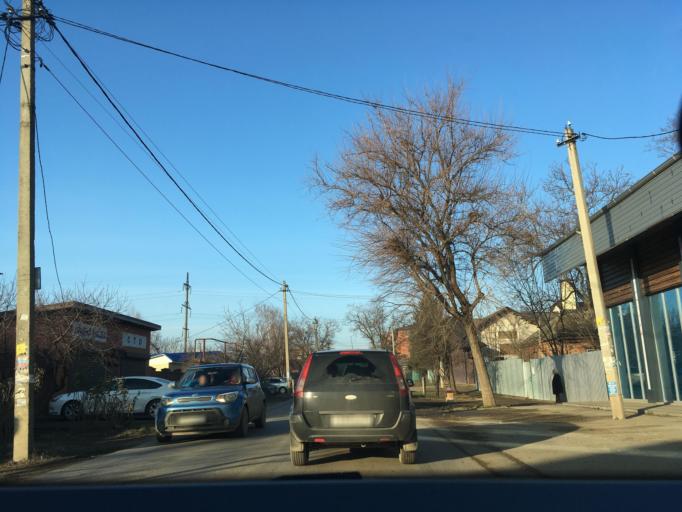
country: RU
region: Krasnodarskiy
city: Krasnodar
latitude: 45.0778
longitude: 39.0208
